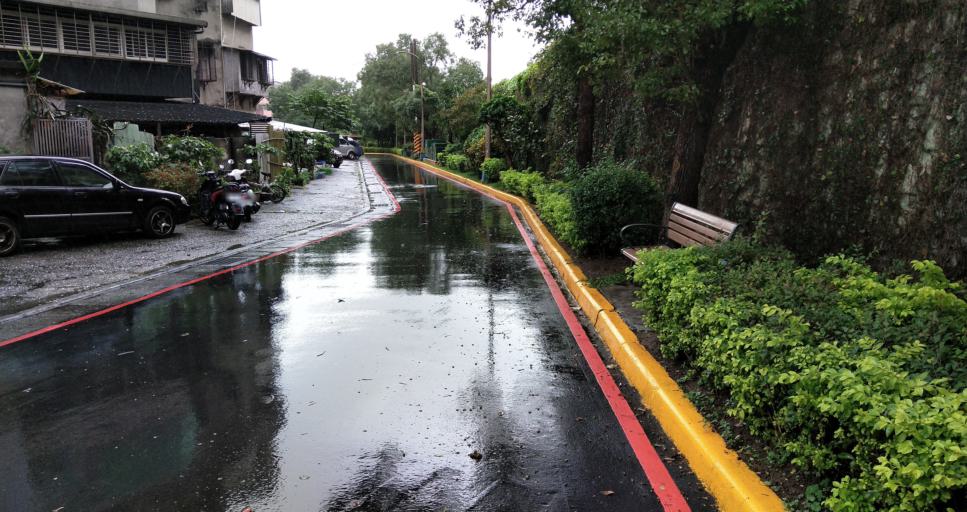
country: TW
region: Taiwan
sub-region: Keelung
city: Keelung
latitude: 25.0721
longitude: 121.6626
